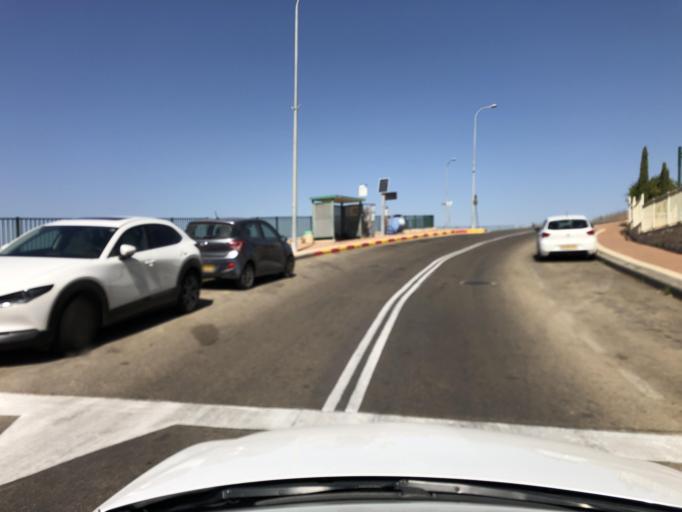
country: PS
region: West Bank
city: An Nabi Ilyas
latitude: 32.1662
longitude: 35.0183
